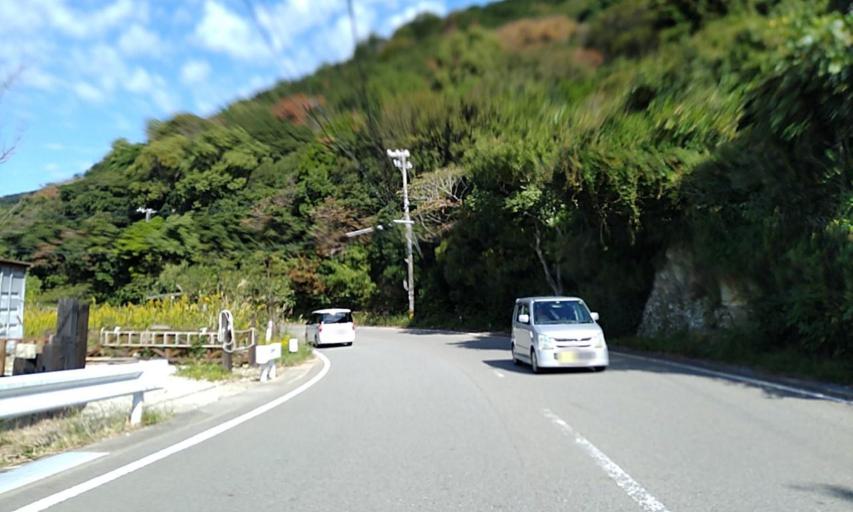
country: JP
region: Wakayama
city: Gobo
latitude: 33.9681
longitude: 135.1178
